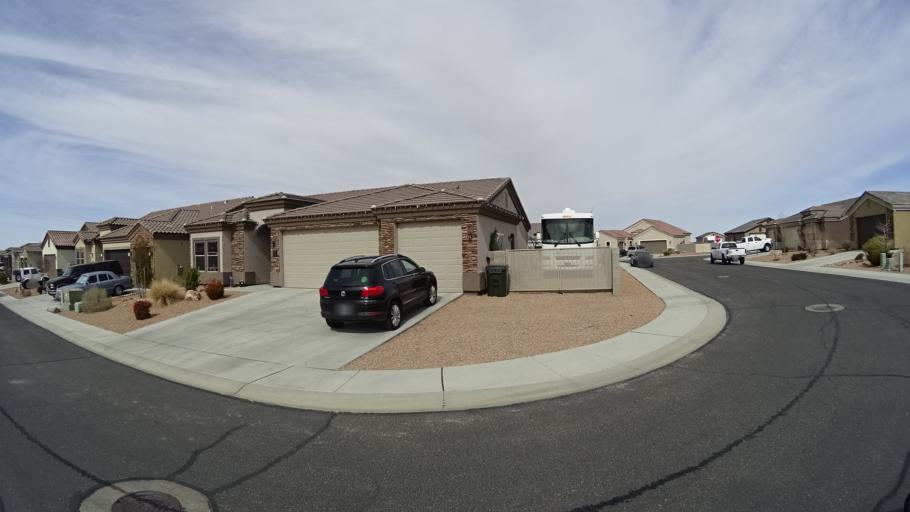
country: US
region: Arizona
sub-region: Mohave County
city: Kingman
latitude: 35.1865
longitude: -114.0163
